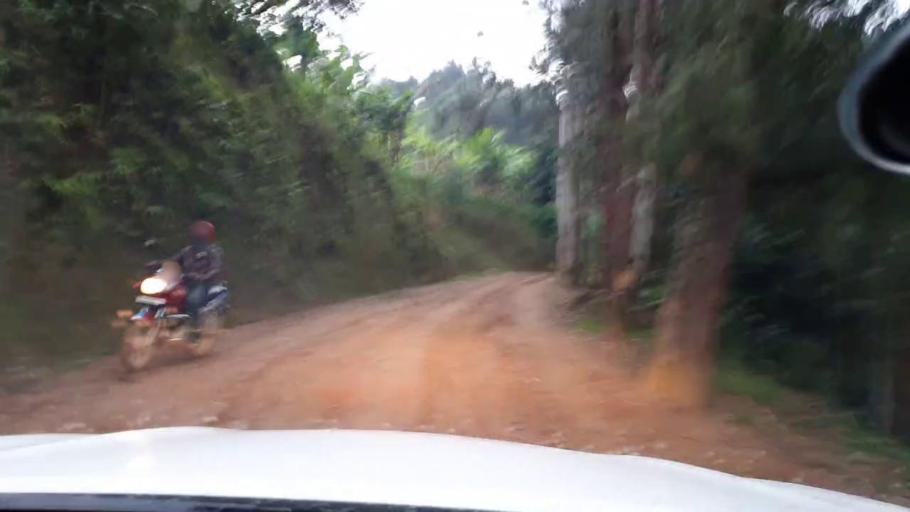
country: RW
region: Western Province
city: Cyangugu
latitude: -2.4101
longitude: 29.1883
